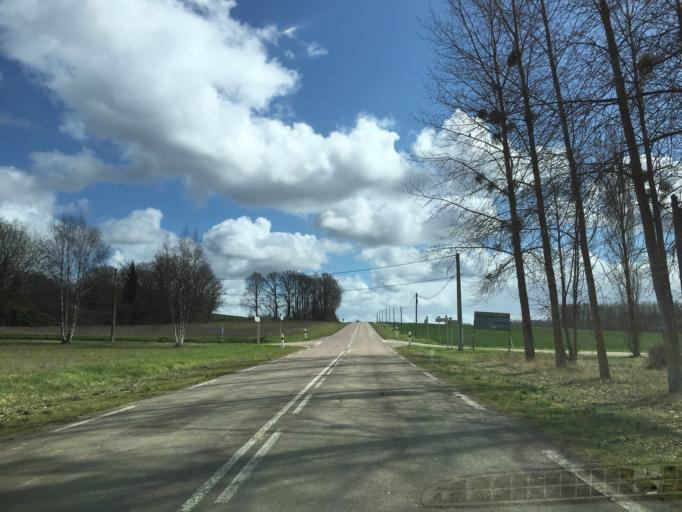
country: FR
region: Bourgogne
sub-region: Departement de l'Yonne
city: Fleury-la-Vallee
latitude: 47.8297
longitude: 3.4170
